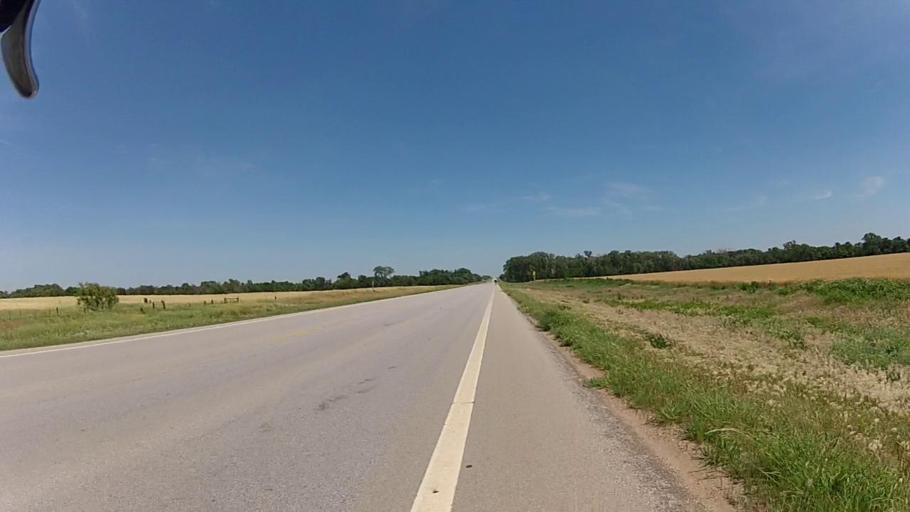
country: US
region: Kansas
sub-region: Harper County
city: Harper
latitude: 37.2388
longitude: -98.1004
